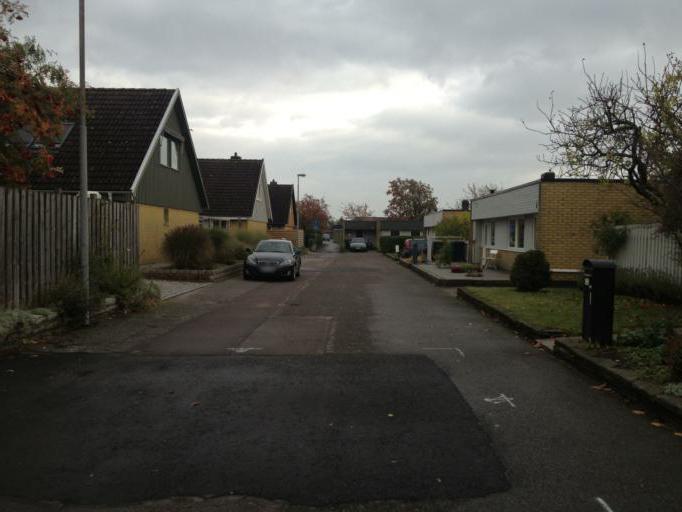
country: SE
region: Skane
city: Bjarred
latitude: 55.7286
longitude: 13.0170
